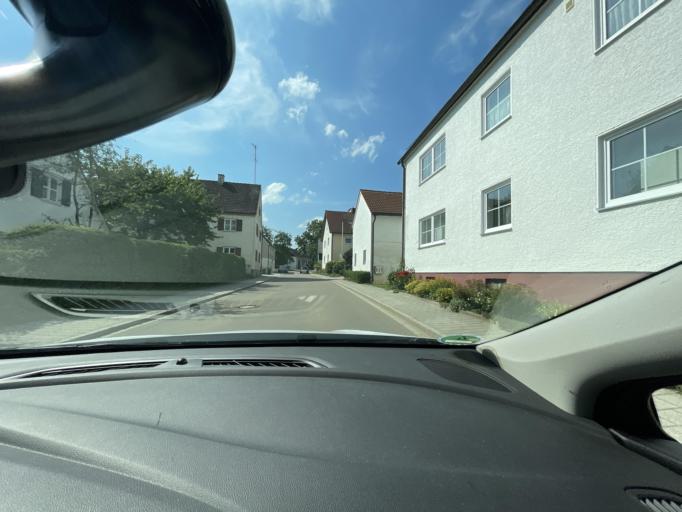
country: DE
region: Bavaria
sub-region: Upper Bavaria
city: Hilgertshausen-Tandern
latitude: 48.4251
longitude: 11.3068
